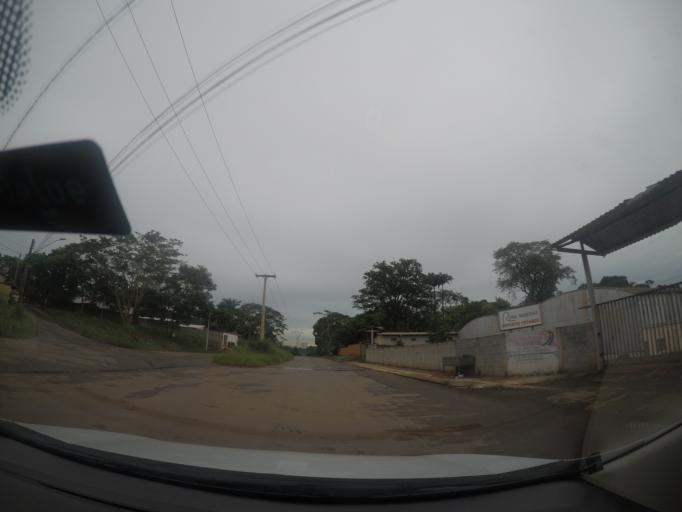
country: BR
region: Goias
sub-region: Goiania
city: Goiania
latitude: -16.6308
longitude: -49.2392
